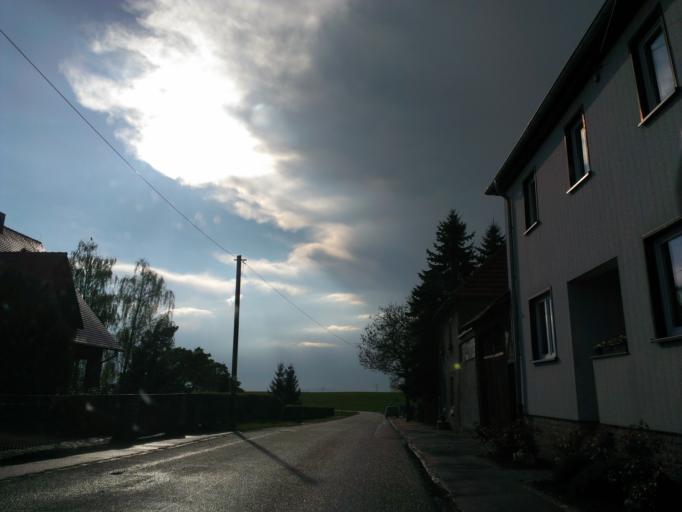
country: DE
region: Thuringia
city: Rockhausen
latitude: 50.9183
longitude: 11.0502
